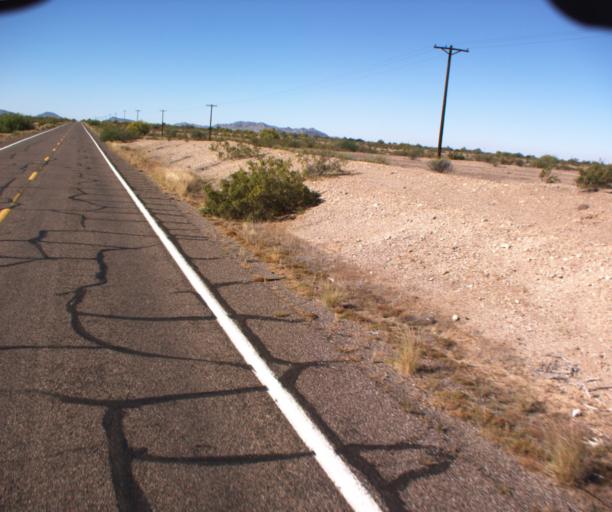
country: US
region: Arizona
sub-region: Maricopa County
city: Gila Bend
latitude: 32.8942
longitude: -112.7467
